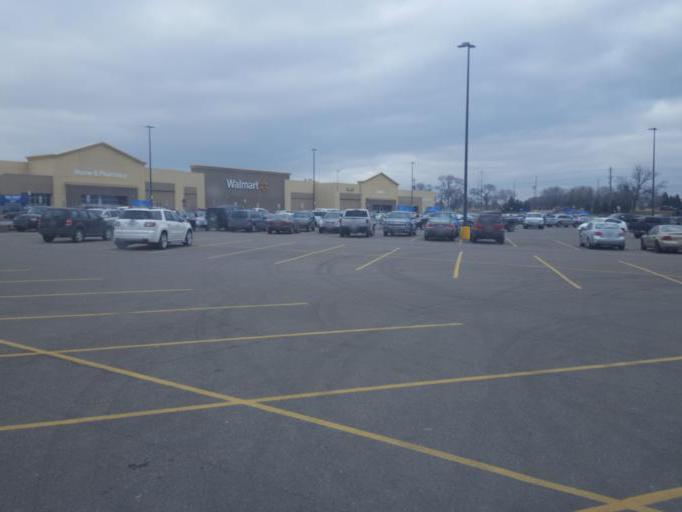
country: US
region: South Dakota
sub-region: Yankton County
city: Yankton
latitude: 42.9065
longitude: -97.3992
